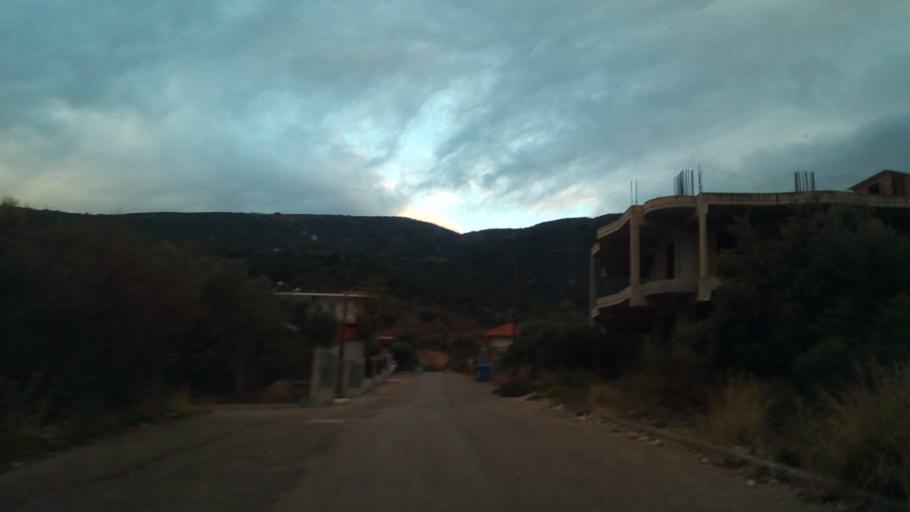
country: GR
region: West Greece
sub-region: Nomos Aitolias kai Akarnanias
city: Nafpaktos
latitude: 38.4111
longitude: 21.8449
